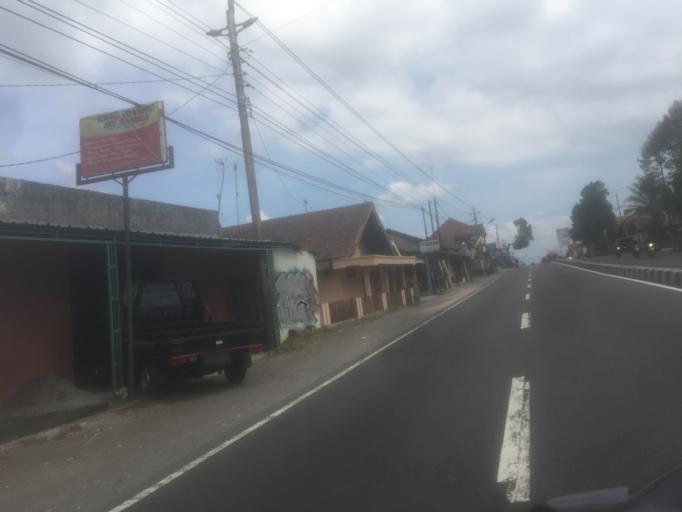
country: ID
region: Central Java
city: Muntilan
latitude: -7.6115
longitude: 110.3053
